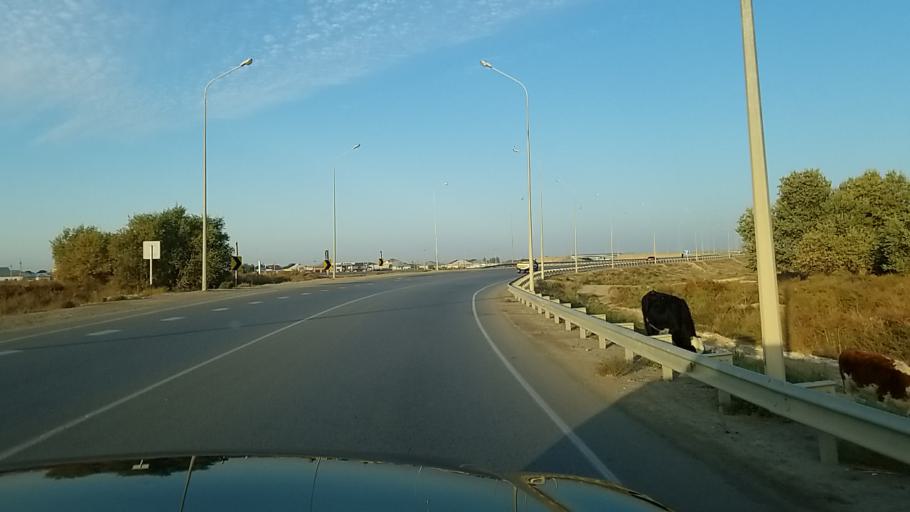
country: KZ
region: Qyzylorda
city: Tasboget
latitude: 44.7718
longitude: 65.4963
